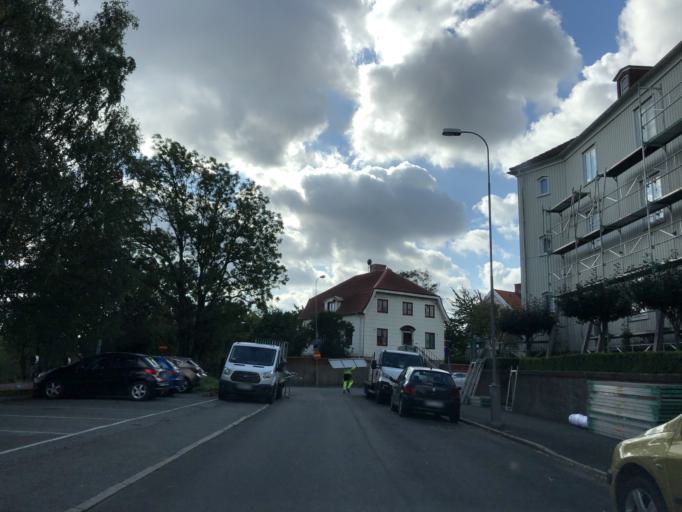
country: SE
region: Vaestra Goetaland
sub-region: Goteborg
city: Eriksbo
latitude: 57.7212
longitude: 12.0216
